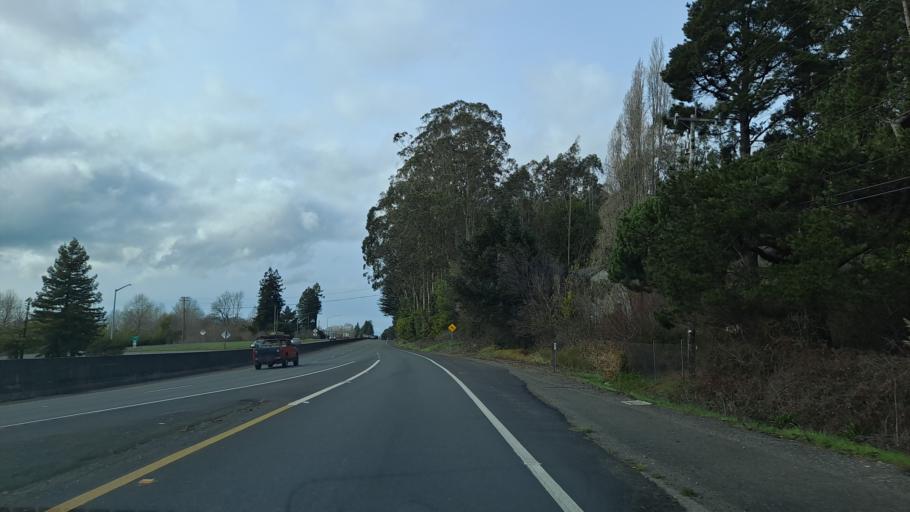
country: US
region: California
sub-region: Humboldt County
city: Fortuna
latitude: 40.6009
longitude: -124.1693
